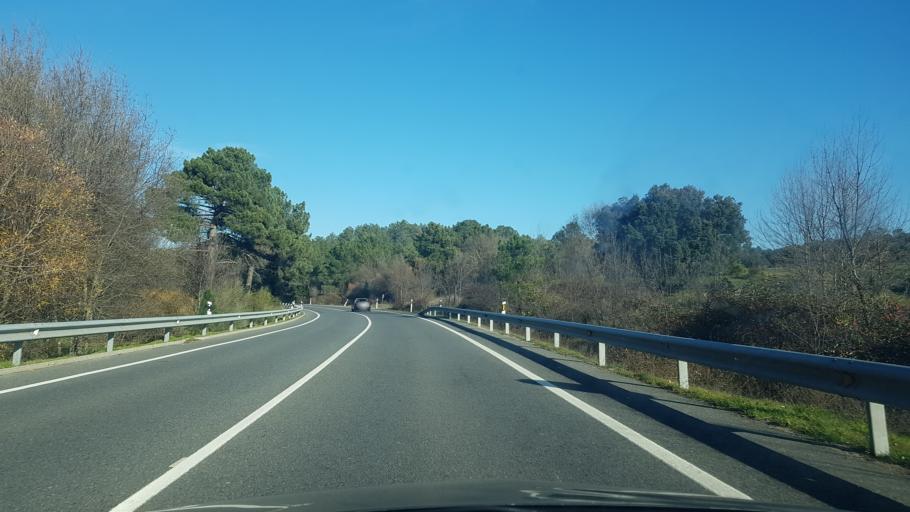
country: ES
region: Madrid
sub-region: Provincia de Madrid
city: Rozas de Puerto Real
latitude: 40.3358
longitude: -4.4639
